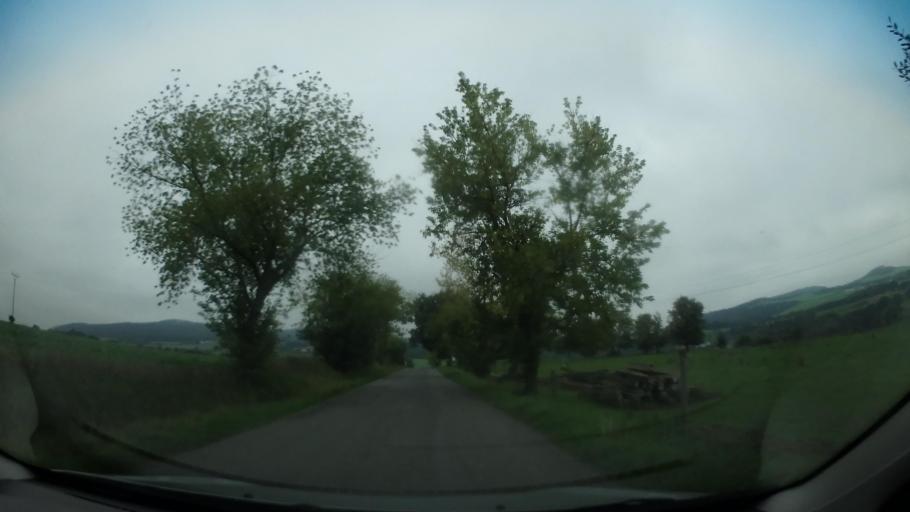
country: CZ
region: Central Bohemia
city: Sedlcany
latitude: 49.7035
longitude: 14.3792
